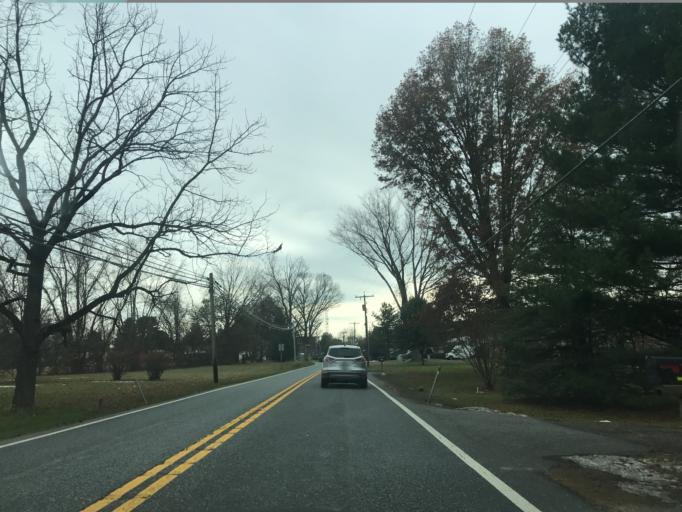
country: US
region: Maryland
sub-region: Harford County
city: Bel Air North
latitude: 39.5862
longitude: -76.3456
